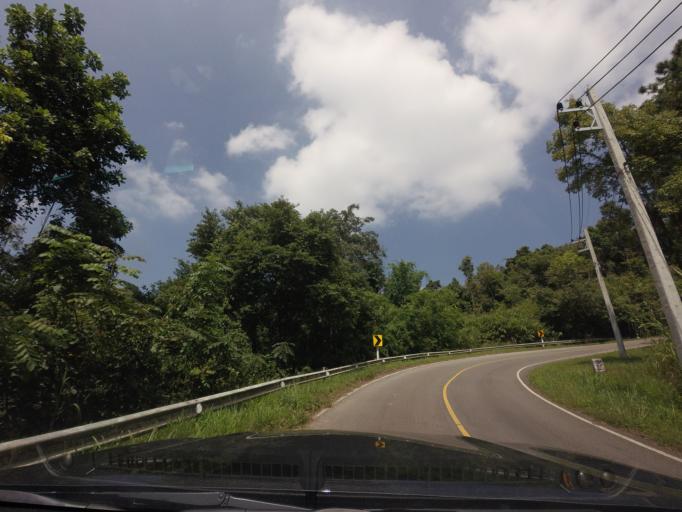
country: TH
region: Loei
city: Na Haeo
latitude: 17.4773
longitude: 100.9164
